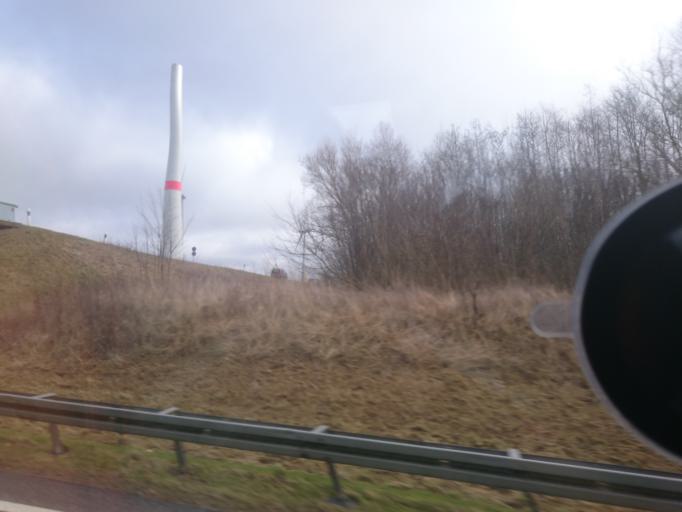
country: DE
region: Mecklenburg-Vorpommern
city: Muhl Rosin
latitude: 53.8279
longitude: 12.3001
